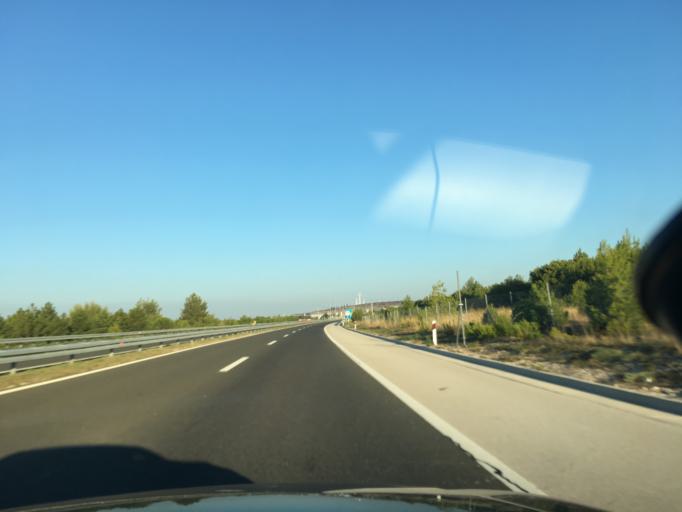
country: HR
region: Sibensko-Kniniska
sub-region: Grad Sibenik
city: Brodarica
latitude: 43.6868
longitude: 16.0463
